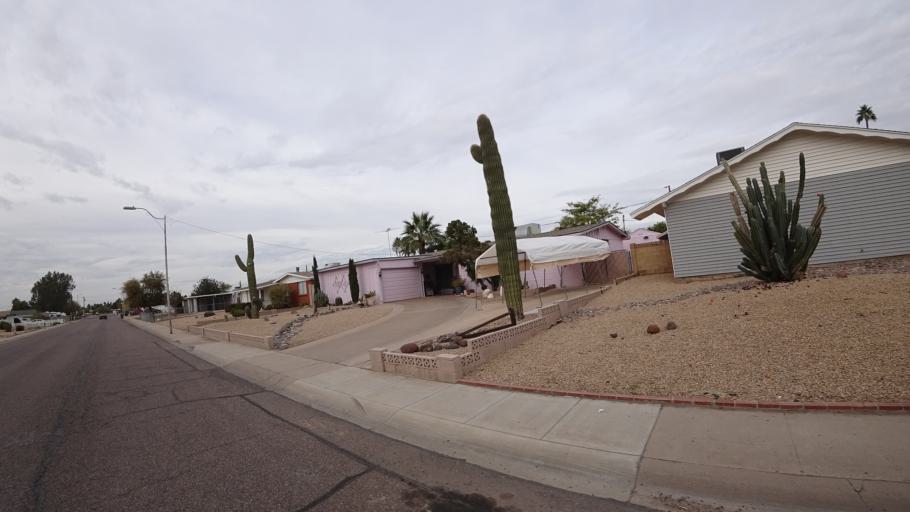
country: US
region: Arizona
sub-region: Maricopa County
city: Glendale
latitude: 33.6200
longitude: -112.1226
